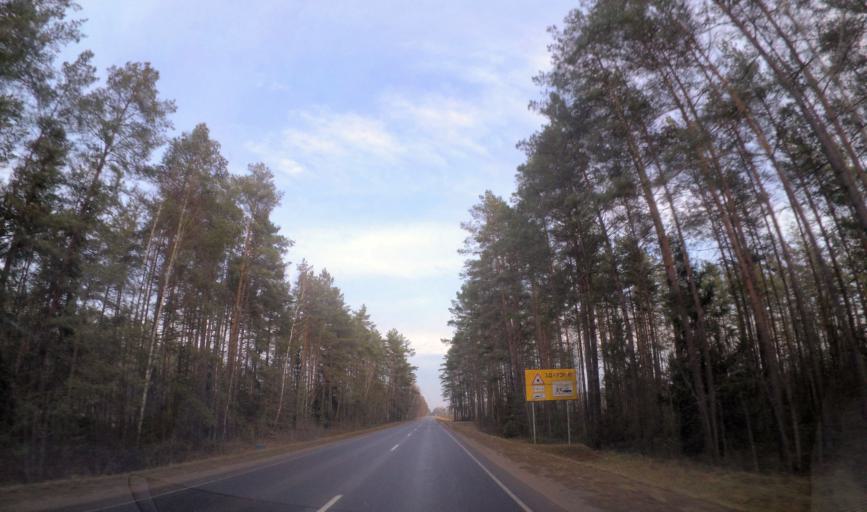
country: LT
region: Alytaus apskritis
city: Druskininkai
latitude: 53.8551
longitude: 24.1007
